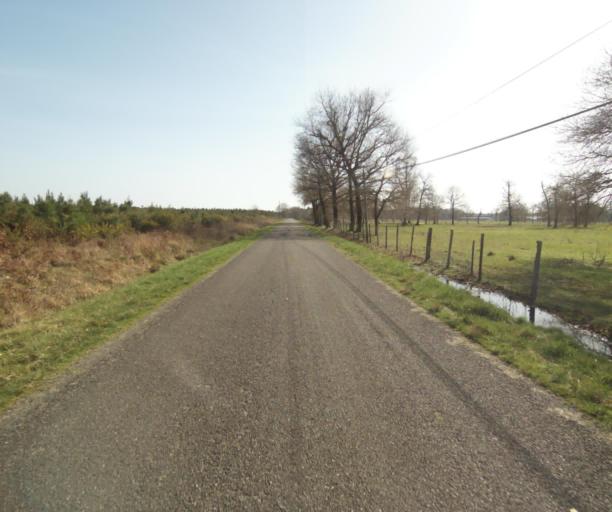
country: FR
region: Aquitaine
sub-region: Departement des Landes
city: Roquefort
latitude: 44.1386
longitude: -0.2617
